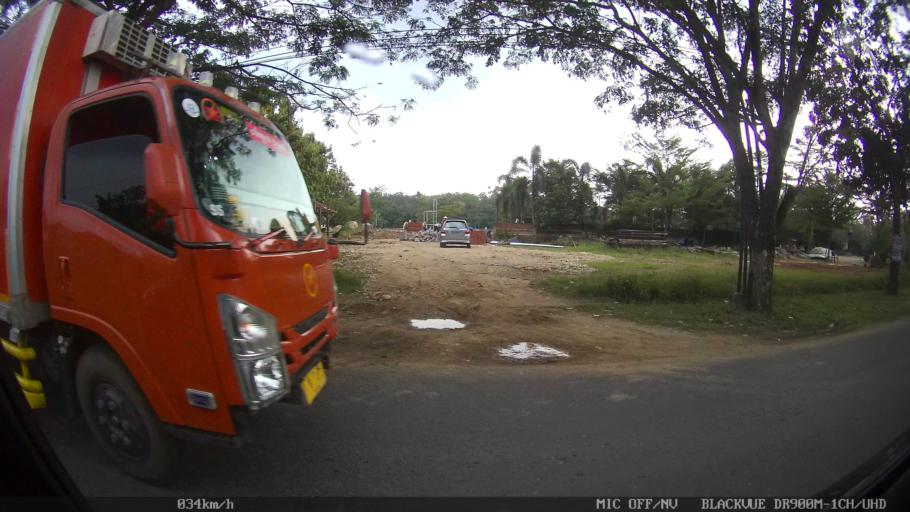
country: ID
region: Lampung
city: Gadingrejo
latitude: -5.3712
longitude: 105.0749
